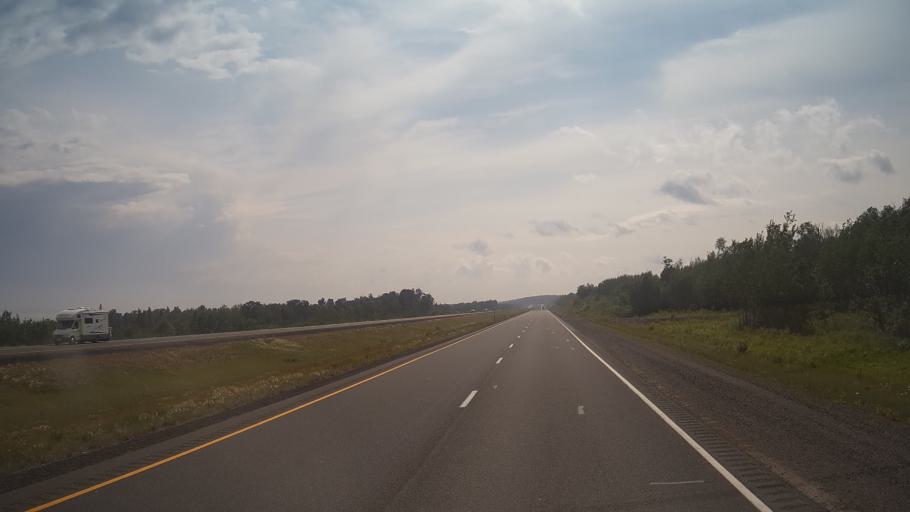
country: CA
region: Ontario
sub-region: Thunder Bay District
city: Thunder Bay
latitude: 48.5641
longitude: -88.8653
